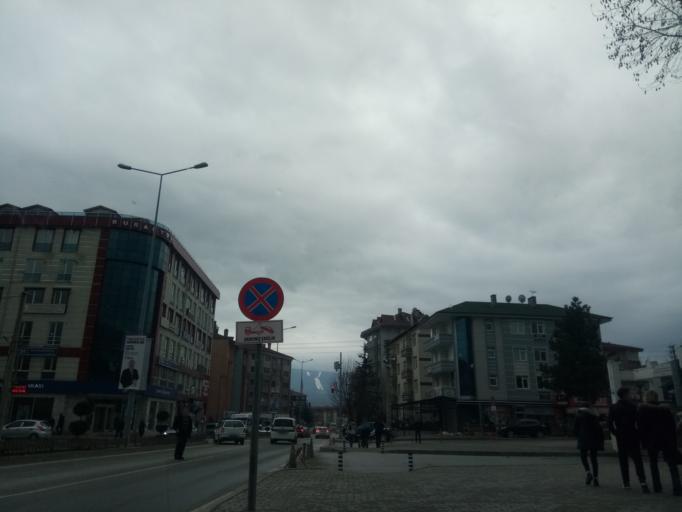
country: TR
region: Bolu
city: Bolu
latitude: 40.7041
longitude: 31.5692
